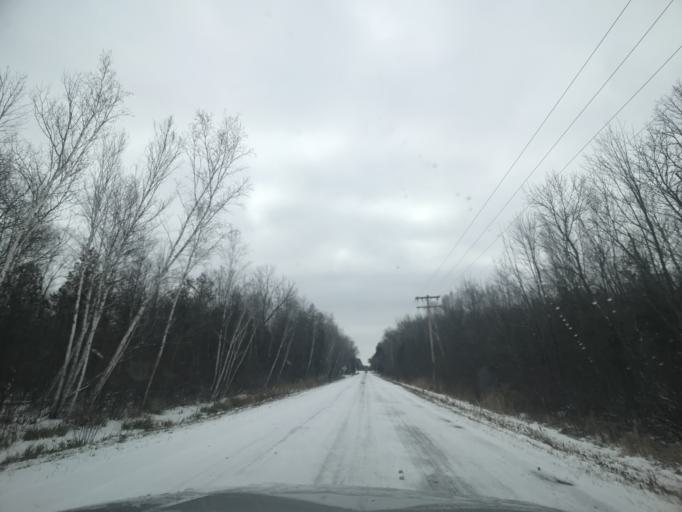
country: US
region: Wisconsin
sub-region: Brown County
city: Suamico
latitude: 44.7052
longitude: -88.1012
